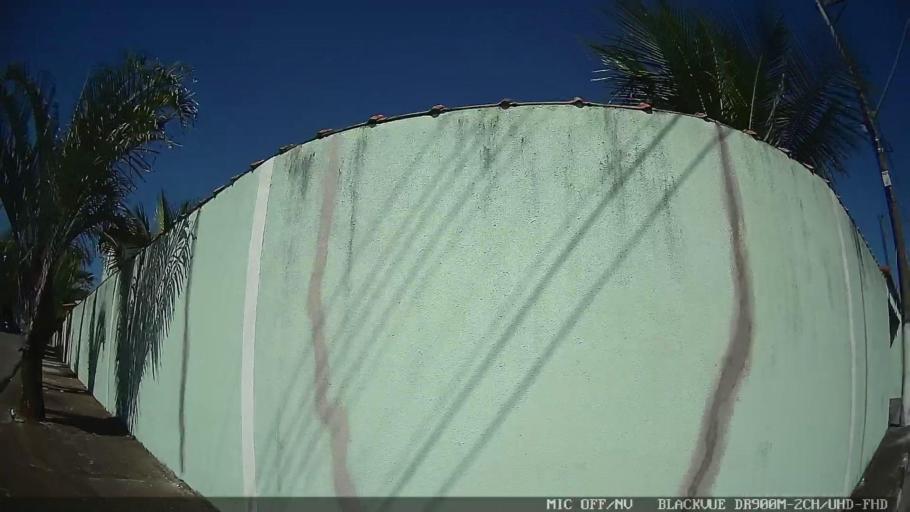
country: BR
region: Sao Paulo
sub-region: Iguape
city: Iguape
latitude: -24.7066
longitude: -47.5632
